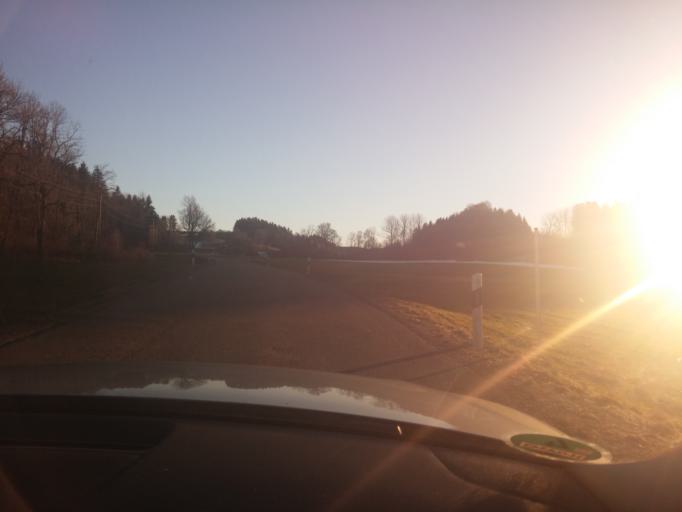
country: DE
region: Bavaria
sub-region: Swabia
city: Altusried
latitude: 47.8141
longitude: 10.1785
